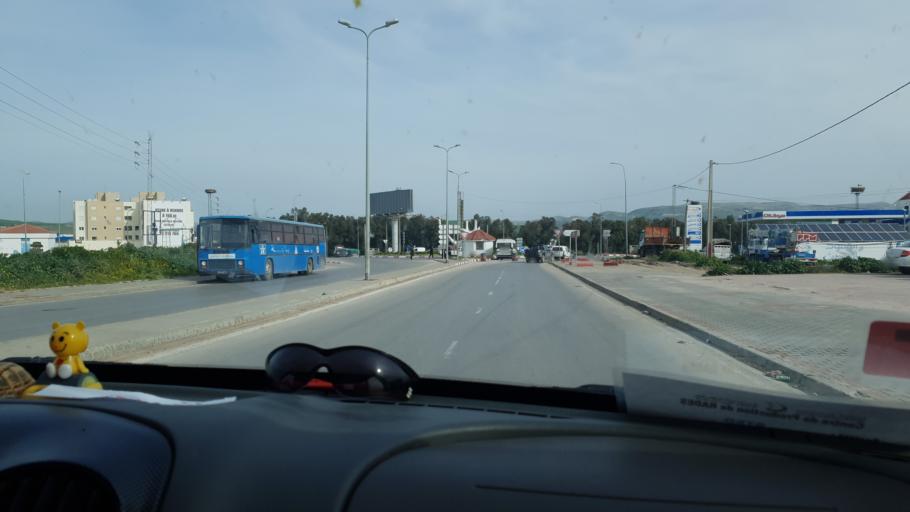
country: TN
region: Bajah
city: Beja
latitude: 36.7289
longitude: 9.2064
